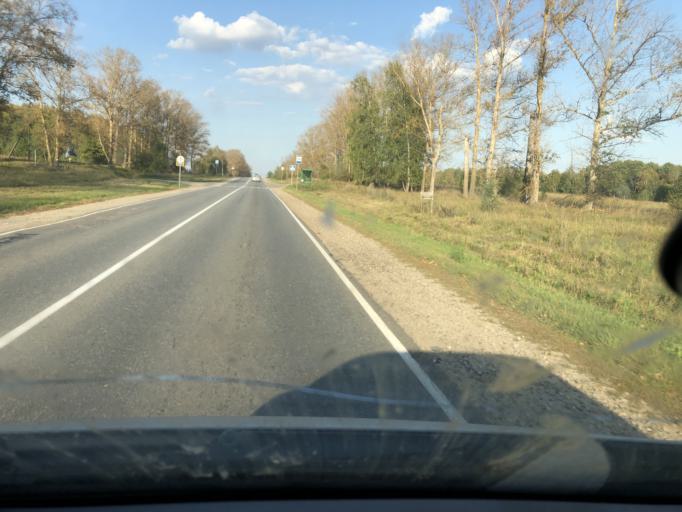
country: RU
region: Kaluga
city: Peremyshl'
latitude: 54.2167
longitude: 36.0177
